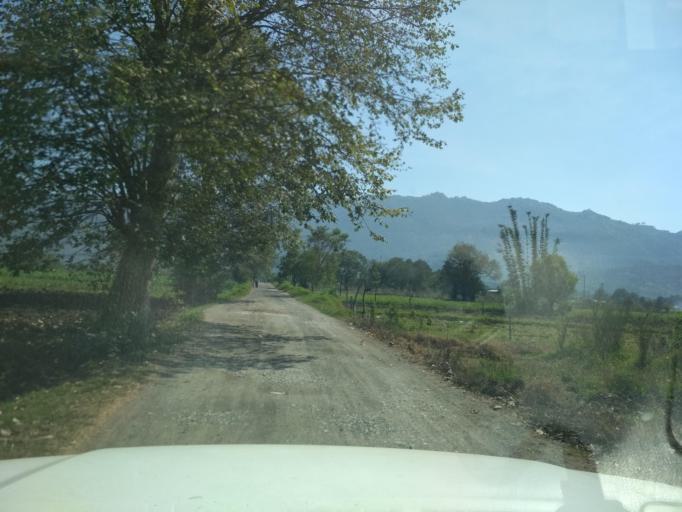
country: MX
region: Veracruz
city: Jalapilla
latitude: 18.8110
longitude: -97.0852
